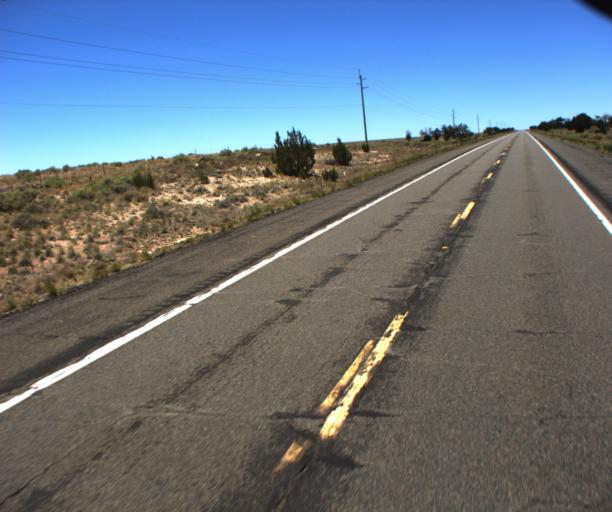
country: US
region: Arizona
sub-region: Coconino County
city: LeChee
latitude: 34.7939
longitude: -110.9878
